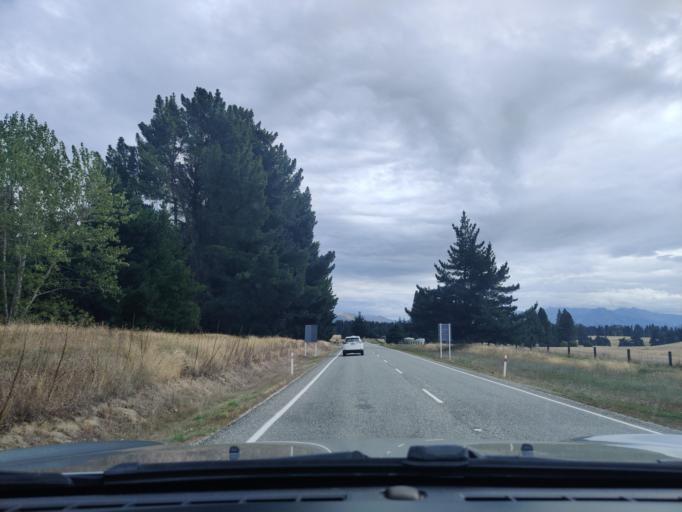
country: NZ
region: Otago
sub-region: Queenstown-Lakes District
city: Wanaka
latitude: -44.7123
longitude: 169.2090
